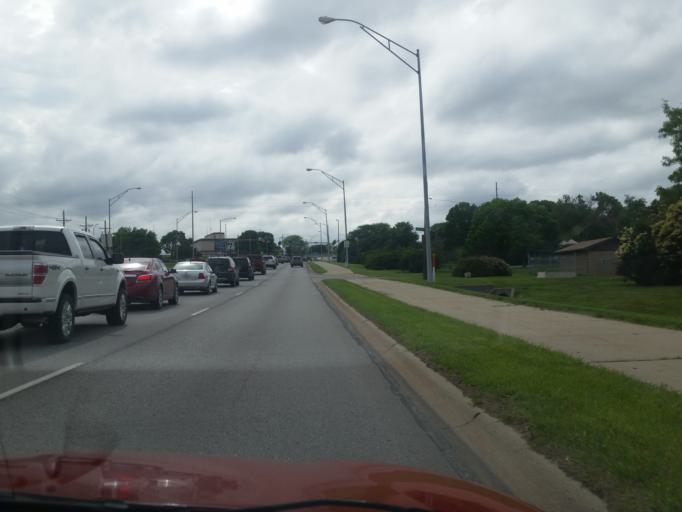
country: US
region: Nebraska
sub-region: Sarpy County
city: Offutt Air Force Base
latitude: 41.1185
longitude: -95.9446
